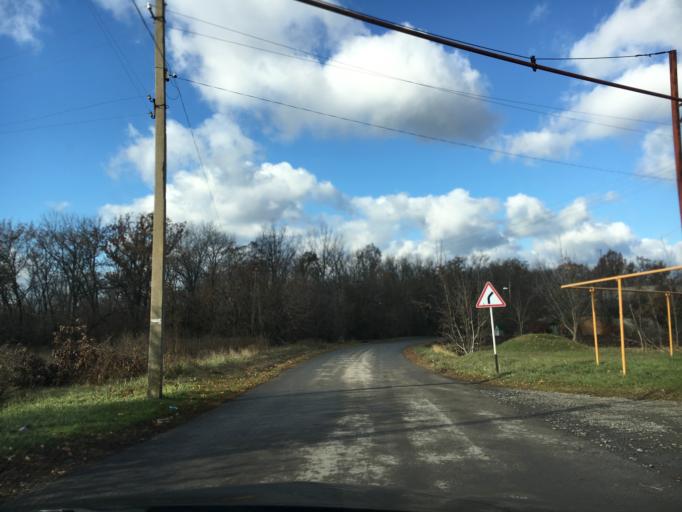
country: RU
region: Rostov
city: Pokrovskoye
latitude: 47.4822
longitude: 38.9140
